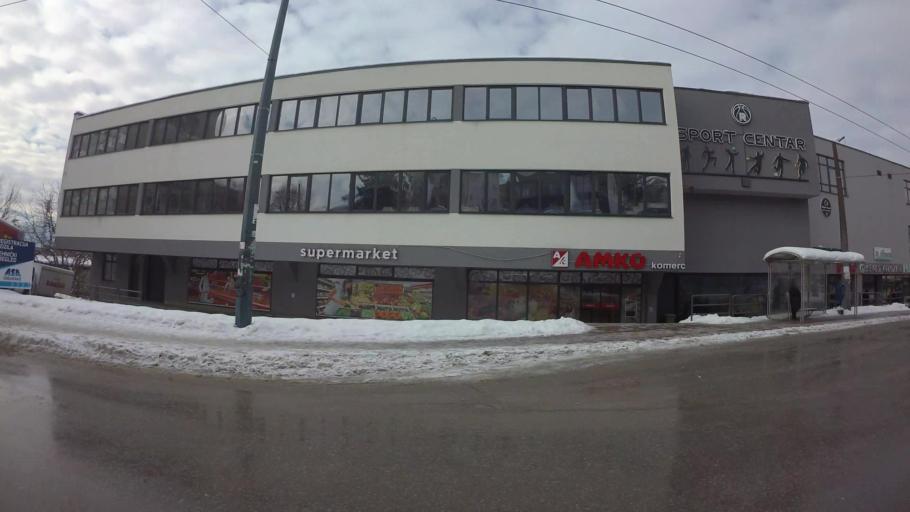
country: BA
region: Federation of Bosnia and Herzegovina
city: Kobilja Glava
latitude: 43.8759
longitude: 18.4126
